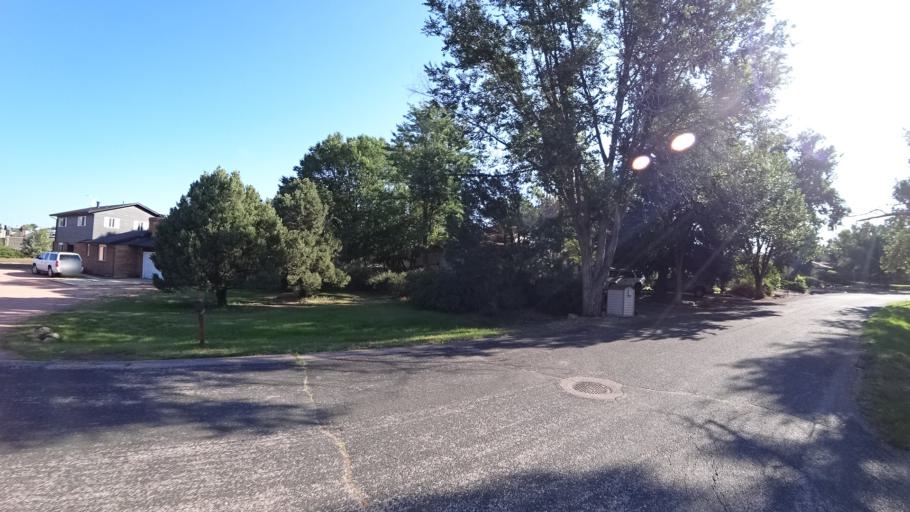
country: US
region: Colorado
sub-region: El Paso County
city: Air Force Academy
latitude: 38.9318
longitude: -104.7925
